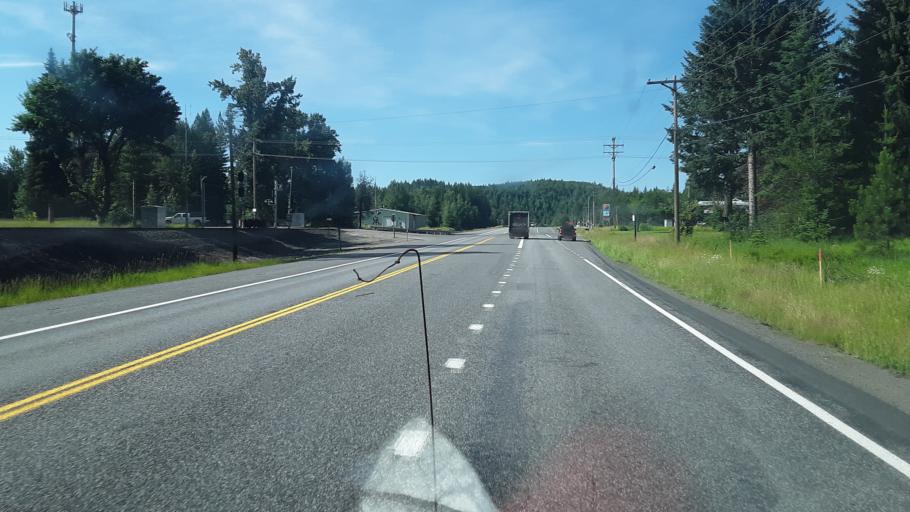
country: US
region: Idaho
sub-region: Bonner County
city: Ponderay
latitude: 48.4303
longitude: -116.4932
